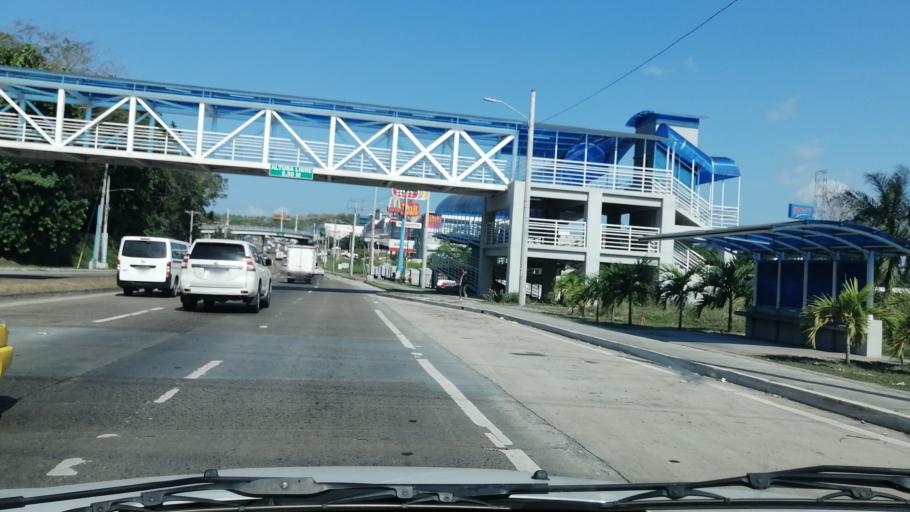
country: PA
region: Panama
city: Panama
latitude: 9.0273
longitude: -79.5296
